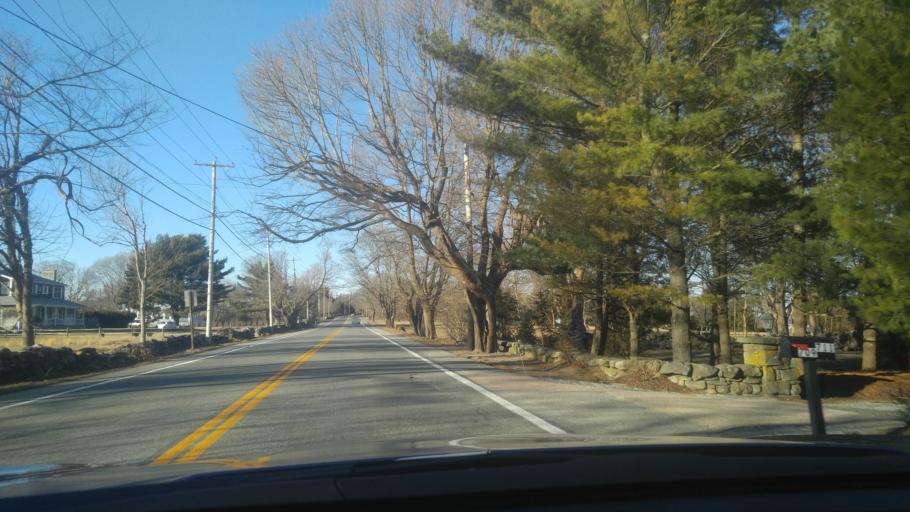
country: US
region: Rhode Island
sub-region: Washington County
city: Narragansett Pier
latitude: 41.4651
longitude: -71.4331
